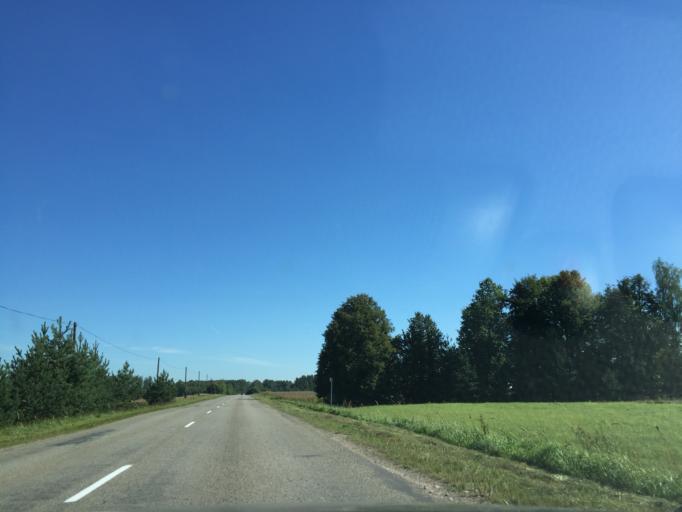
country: LV
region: Akniste
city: Akniste
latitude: 56.1447
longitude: 25.7978
